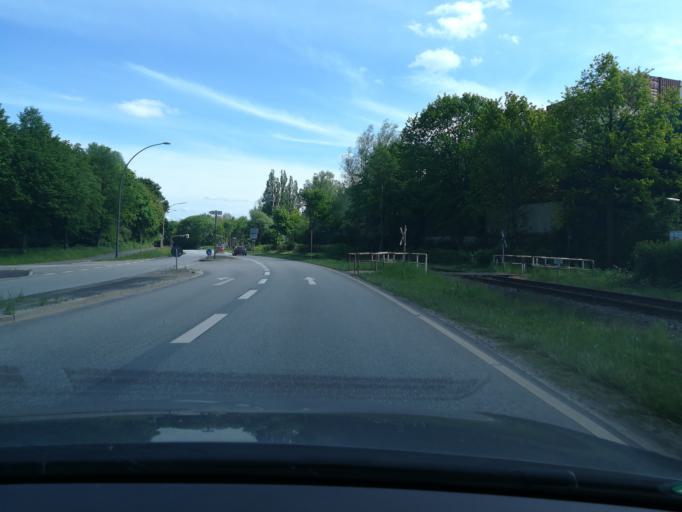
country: DE
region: Hamburg
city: Kleiner Grasbrook
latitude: 53.5022
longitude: 9.9844
